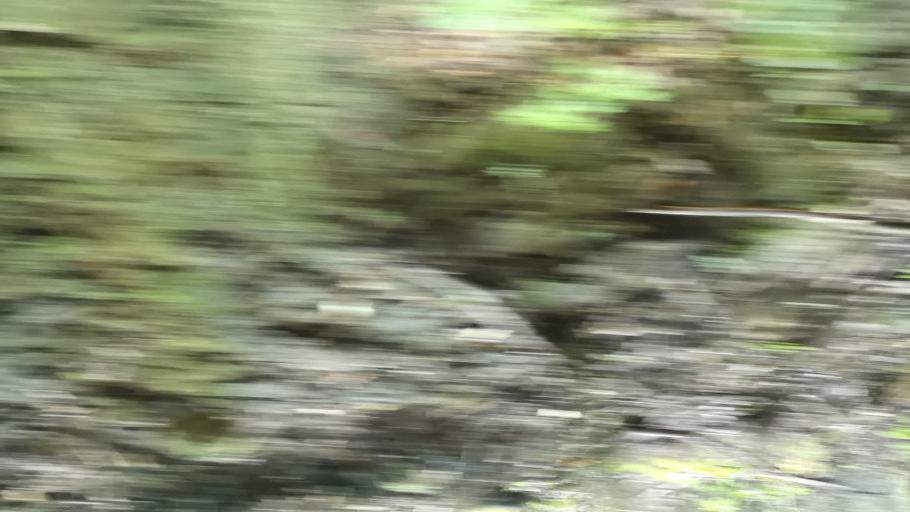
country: ES
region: Canary Islands
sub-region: Provincia de Santa Cruz de Tenerife
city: Vallehermosa
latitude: 28.1610
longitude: -17.2986
